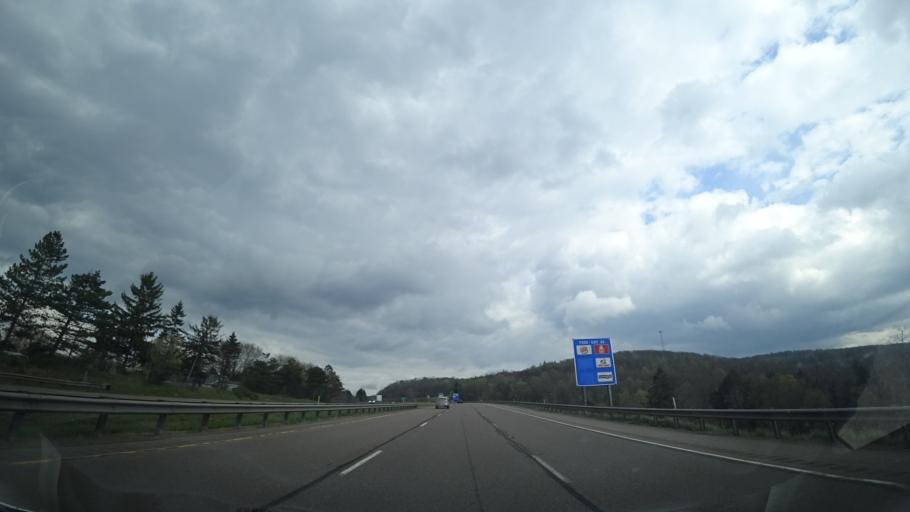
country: US
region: Pennsylvania
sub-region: Somerset County
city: Meyersdale
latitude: 39.6954
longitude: -79.1345
